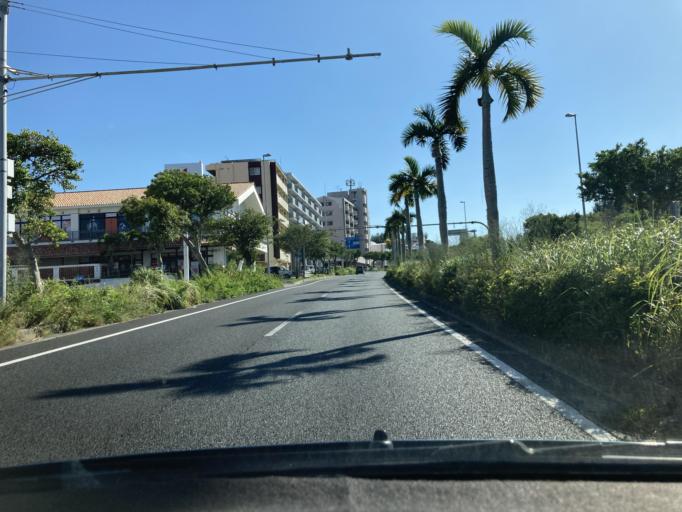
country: JP
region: Okinawa
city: Naha-shi
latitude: 26.2009
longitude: 127.6619
